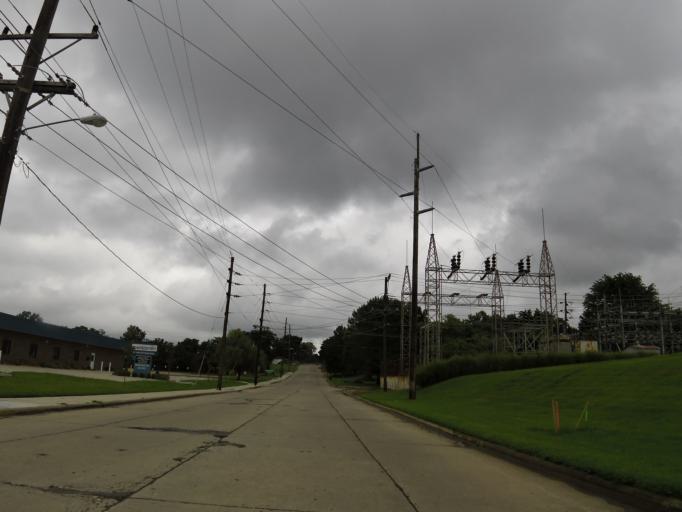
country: US
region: Missouri
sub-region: Cape Girardeau County
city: Cape Girardeau
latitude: 37.3174
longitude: -89.5467
